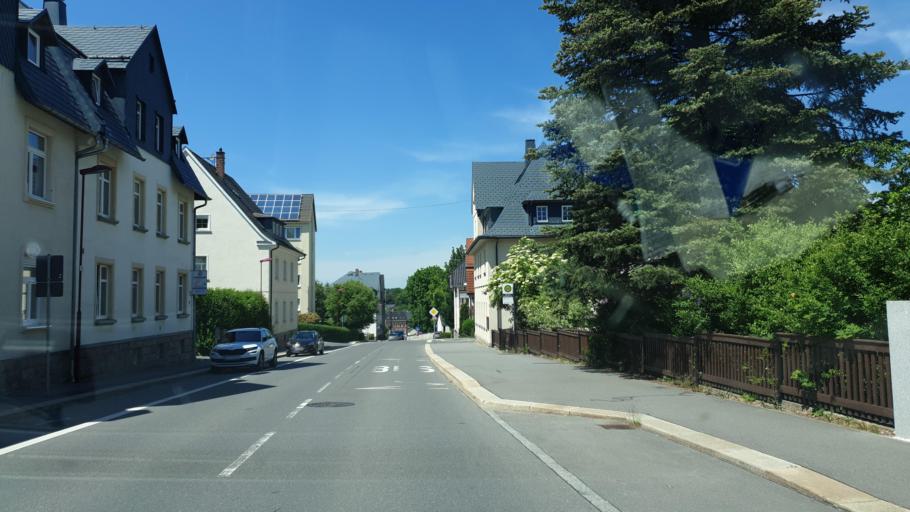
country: DE
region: Saxony
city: Rodewisch
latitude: 50.5285
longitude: 12.4093
